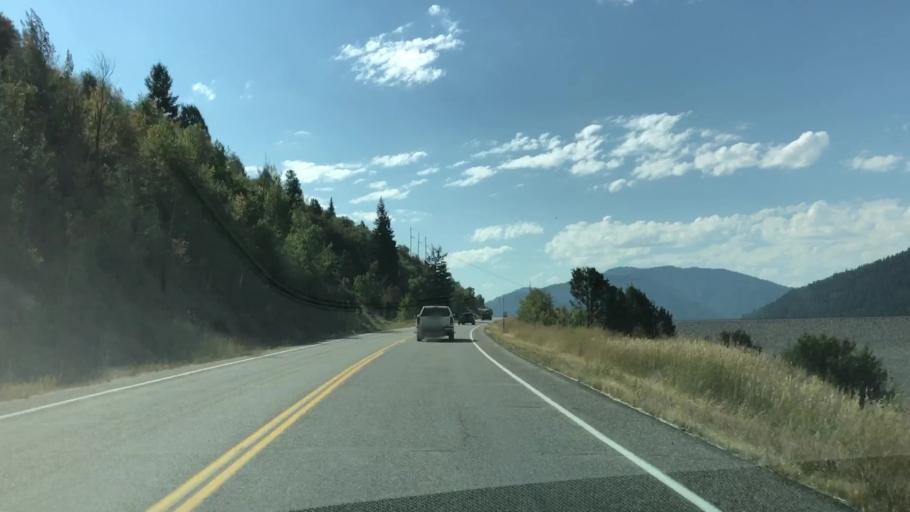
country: US
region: Idaho
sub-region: Teton County
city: Victor
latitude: 43.3395
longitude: -111.2006
